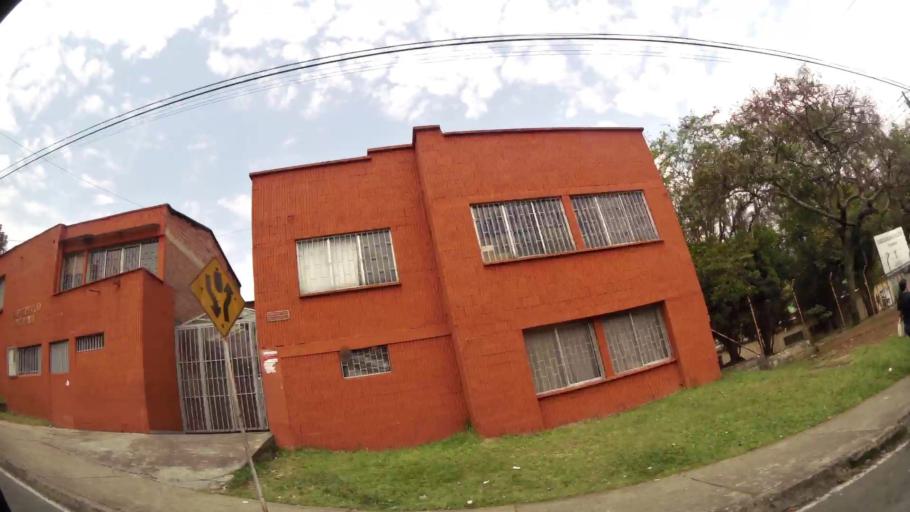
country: CO
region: Antioquia
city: Medellin
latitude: 6.2465
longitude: -75.6163
